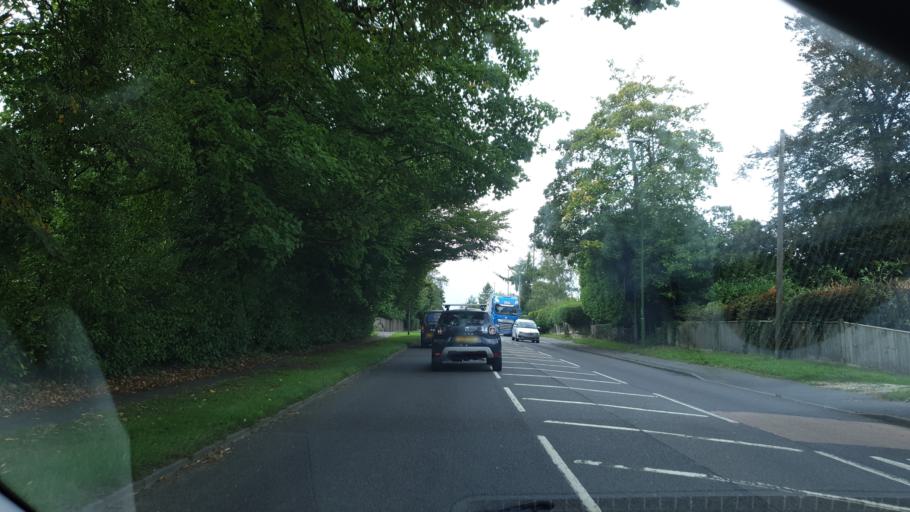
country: GB
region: England
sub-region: East Sussex
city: Forest Row
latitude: 51.1138
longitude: 0.0181
